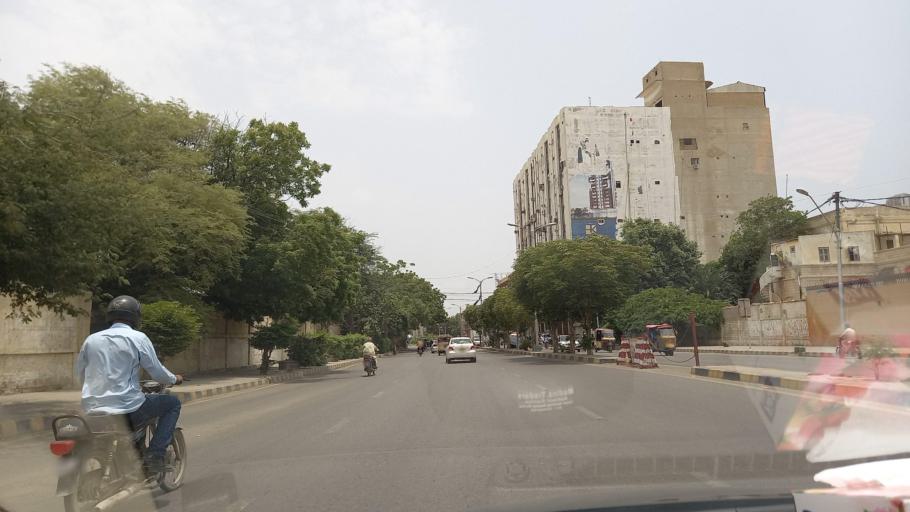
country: PK
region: Sindh
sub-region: Karachi District
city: Karachi
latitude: 24.8525
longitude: 67.0291
